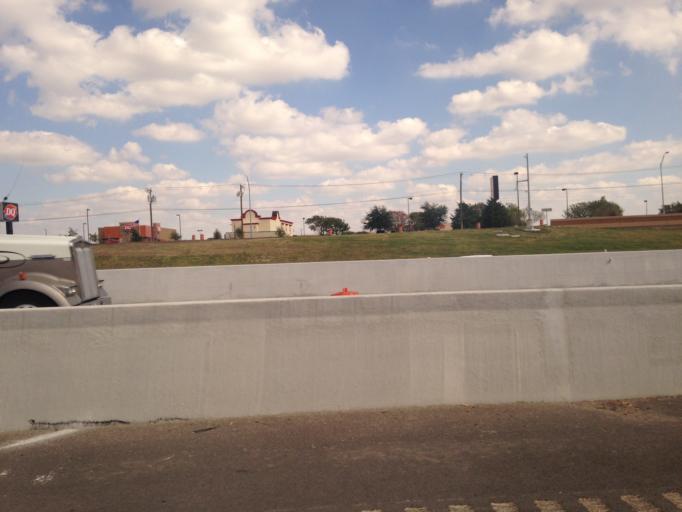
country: US
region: Texas
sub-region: Tarrant County
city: Blue Mound
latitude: 32.8703
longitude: -97.3165
